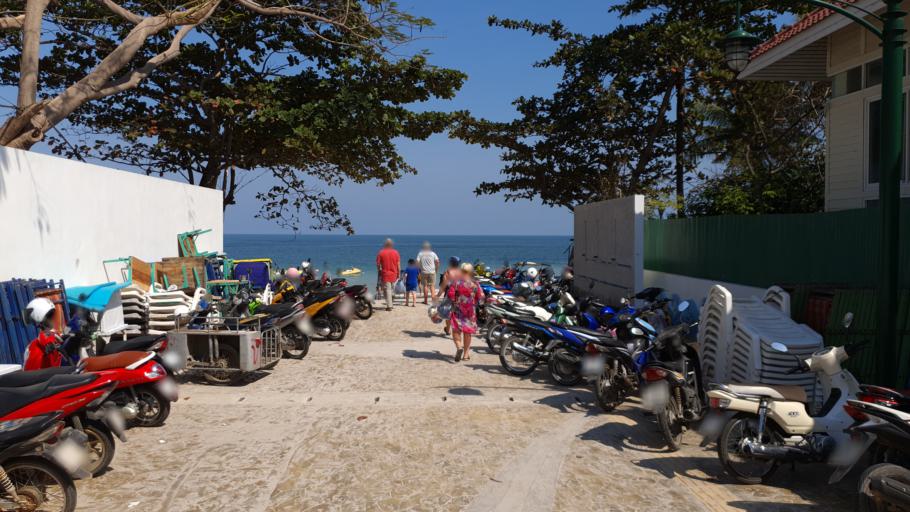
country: TH
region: Prachuap Khiri Khan
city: Hua Hin
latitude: 12.5695
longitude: 99.9624
